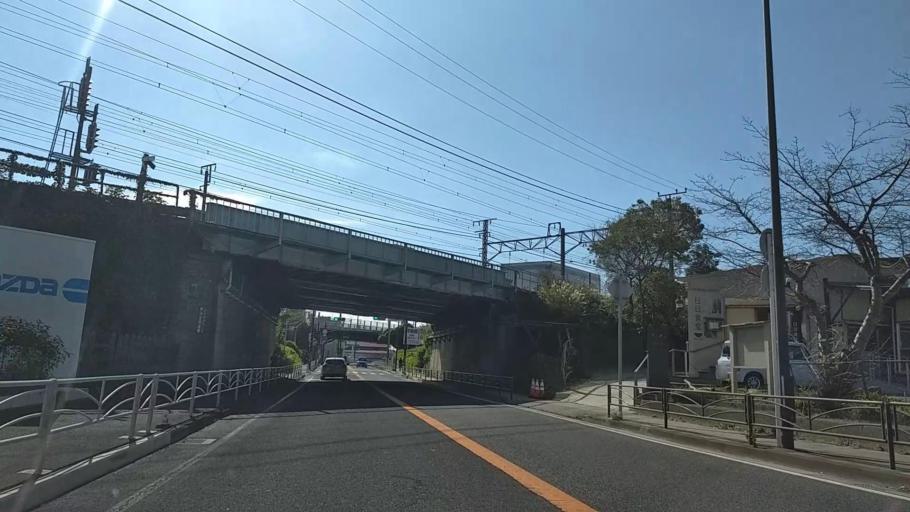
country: JP
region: Kanagawa
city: Hiratsuka
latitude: 35.3176
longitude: 139.3228
